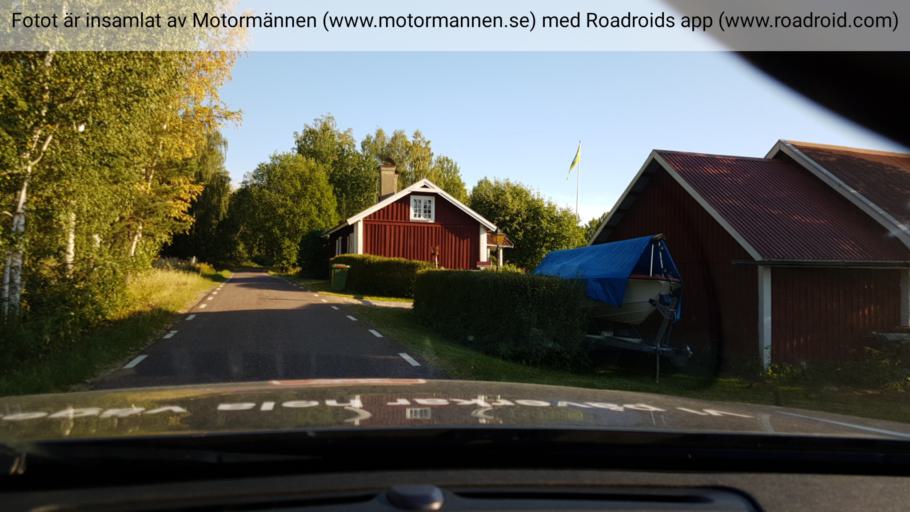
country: SE
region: Vaestmanland
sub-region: Surahammars Kommun
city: Surahammar
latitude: 59.6742
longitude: 16.0763
